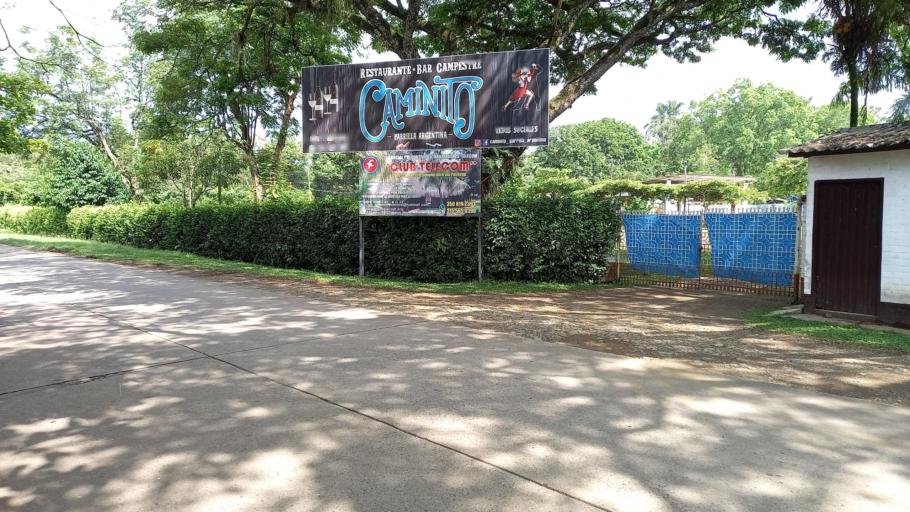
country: CO
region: Valle del Cauca
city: Jamundi
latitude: 3.2362
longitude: -76.5714
